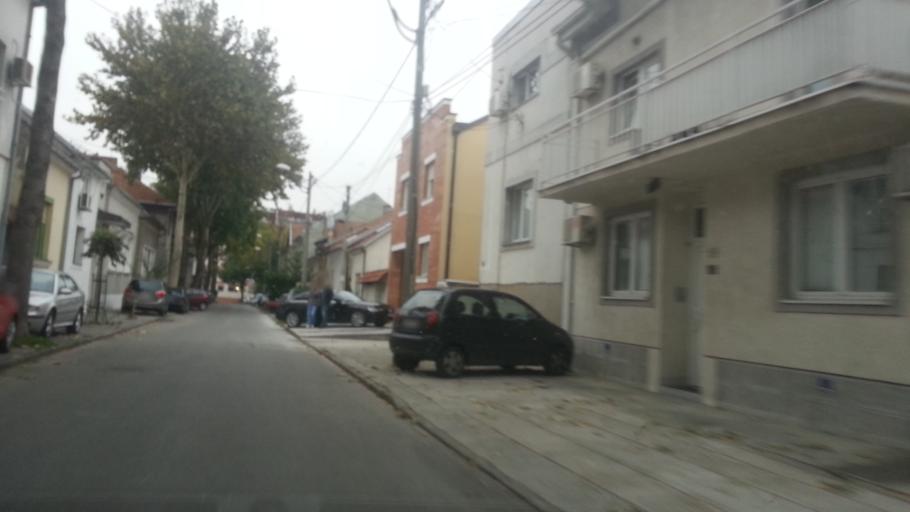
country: RS
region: Central Serbia
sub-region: Belgrade
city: Zemun
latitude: 44.8401
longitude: 20.3991
